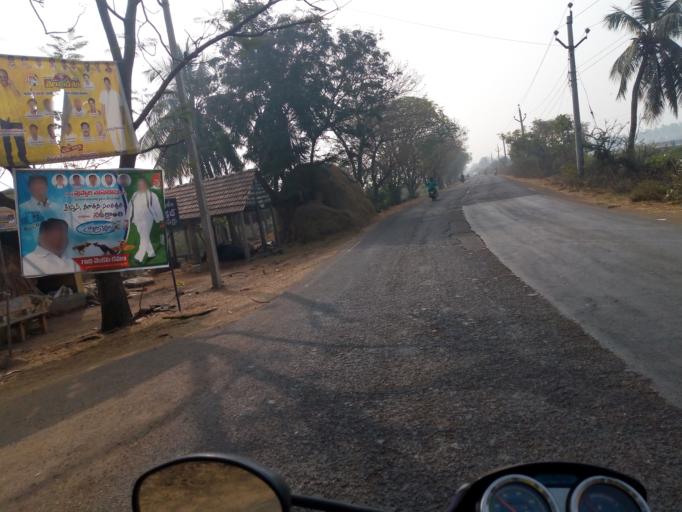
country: IN
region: Andhra Pradesh
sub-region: West Godavari
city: Tadepallegudem
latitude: 16.7915
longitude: 81.4187
